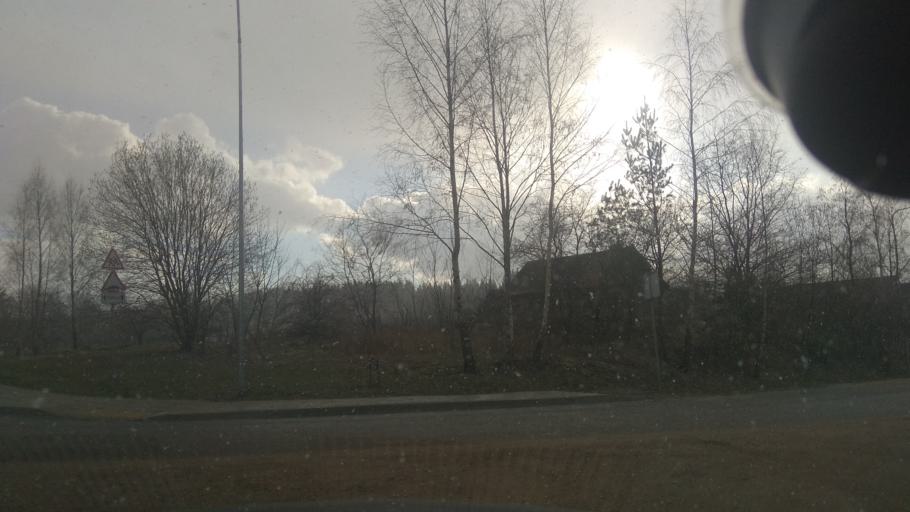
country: LT
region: Vilnius County
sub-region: Vilnius
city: Fabijoniskes
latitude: 54.7469
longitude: 25.2513
